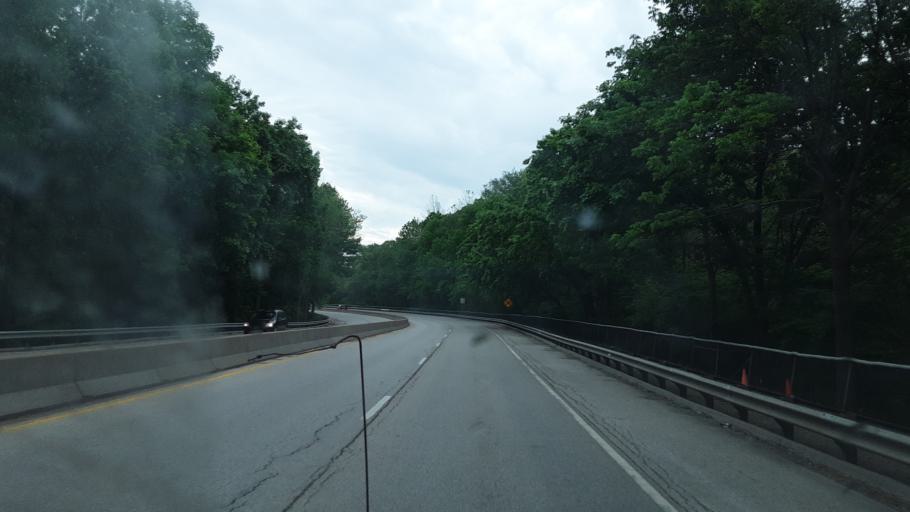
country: US
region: Iowa
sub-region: Lee County
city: Keokuk
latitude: 40.3889
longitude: -91.3683
